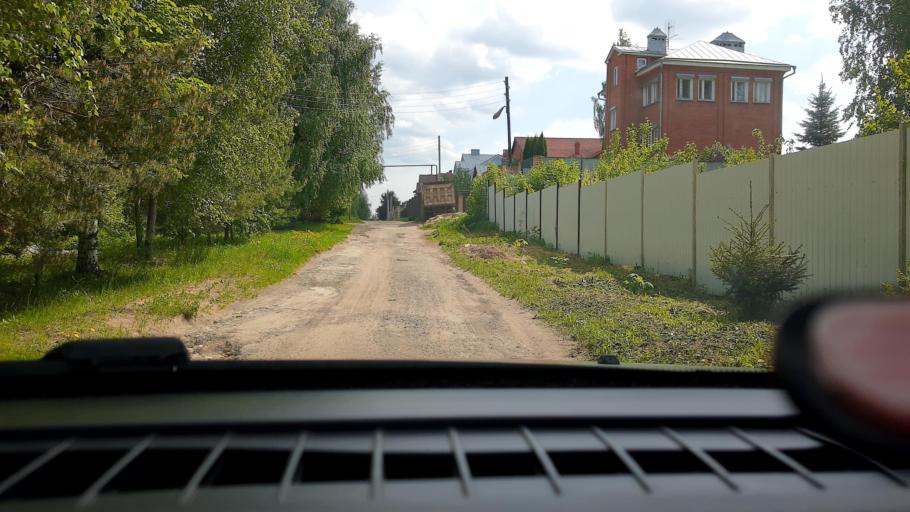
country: RU
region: Nizjnij Novgorod
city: Afonino
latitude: 56.2070
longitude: 44.1477
